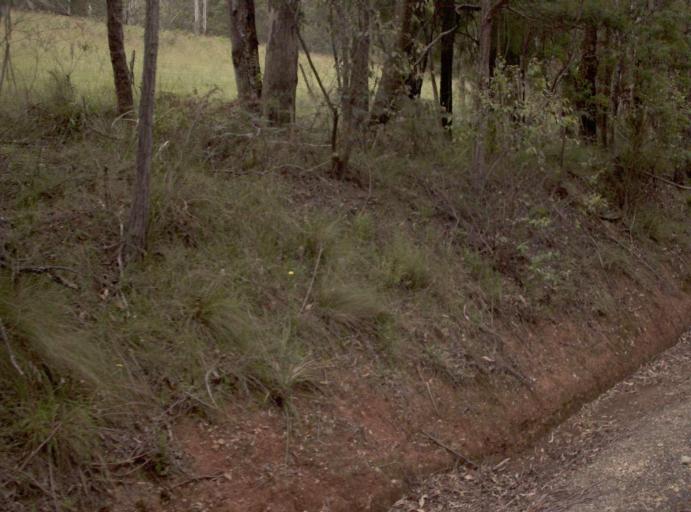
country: AU
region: New South Wales
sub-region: Bombala
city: Bombala
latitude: -37.4030
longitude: 149.2000
